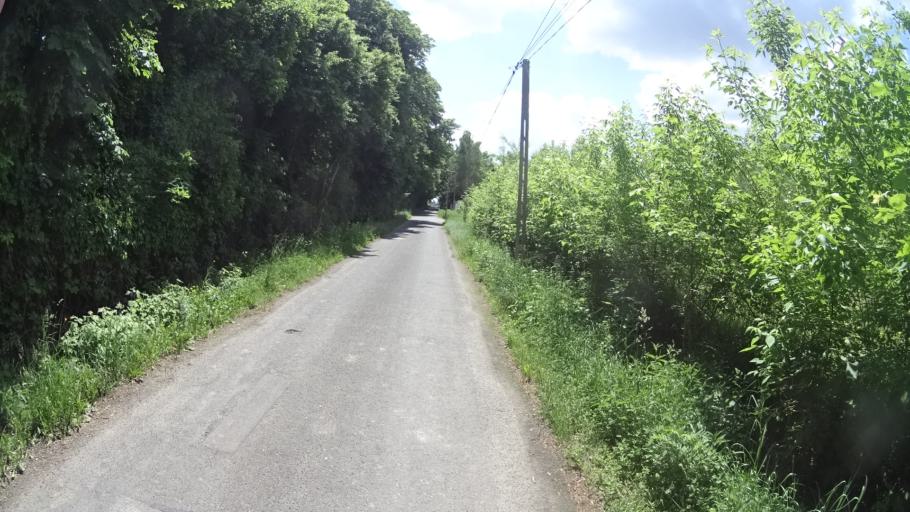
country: PL
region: Masovian Voivodeship
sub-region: Powiat warszawski zachodni
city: Ozarow Mazowiecki
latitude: 52.2297
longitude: 20.7622
